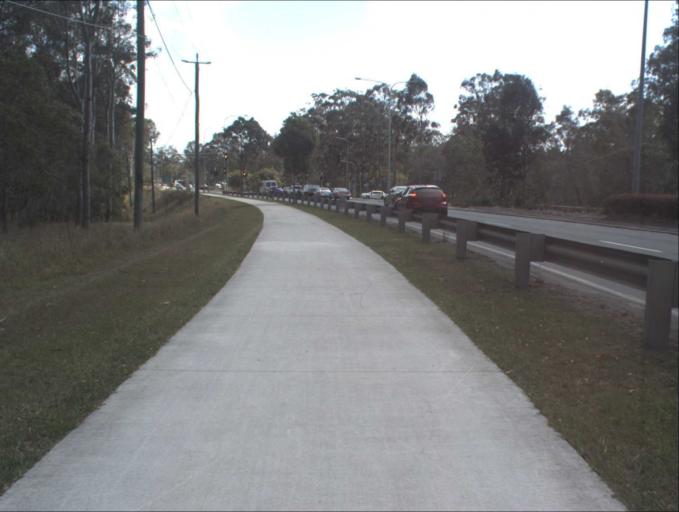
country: AU
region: Queensland
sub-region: Logan
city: Slacks Creek
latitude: -27.6564
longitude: 153.1438
